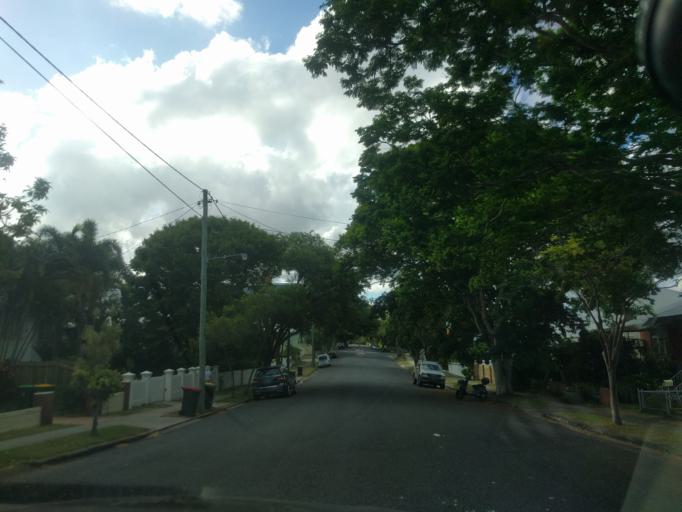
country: AU
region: Queensland
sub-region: Brisbane
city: Brisbane
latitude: -27.4716
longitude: 153.0467
